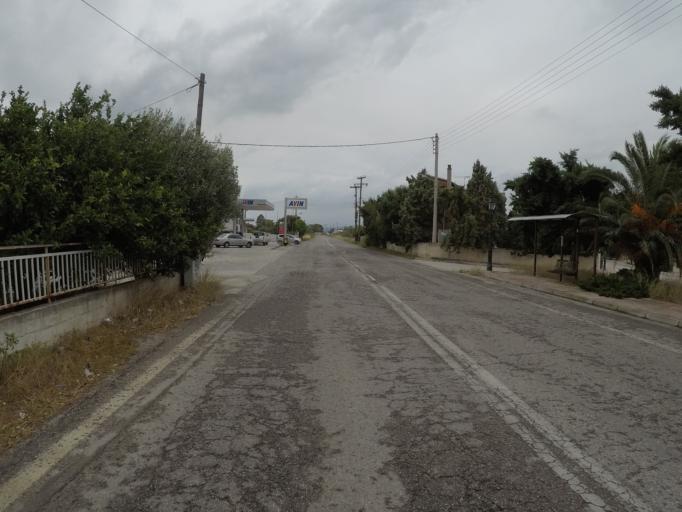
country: GR
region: Peloponnese
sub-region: Nomos Korinthias
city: Isthmia
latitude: 37.9246
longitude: 23.0199
